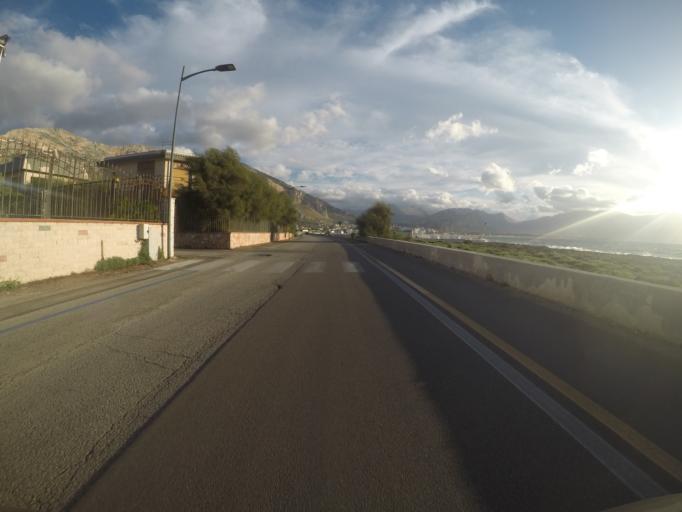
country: IT
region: Sicily
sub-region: Palermo
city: Isola delle Femmine
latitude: 38.1966
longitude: 13.2437
